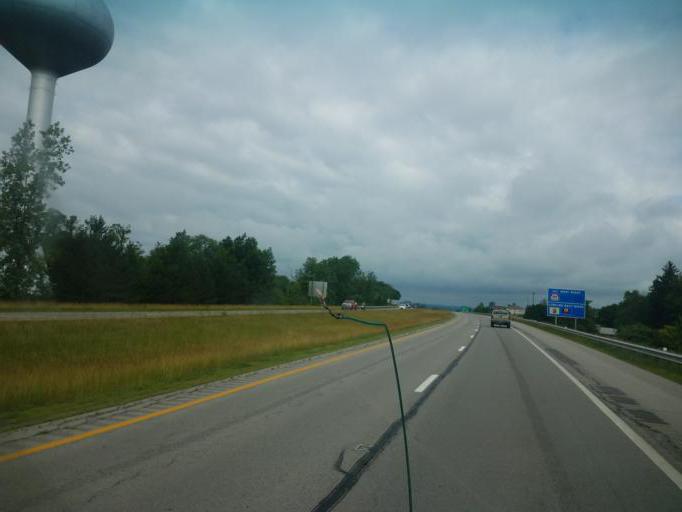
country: US
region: Ohio
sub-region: Logan County
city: Bellefontaine
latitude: 40.3776
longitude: -83.7443
